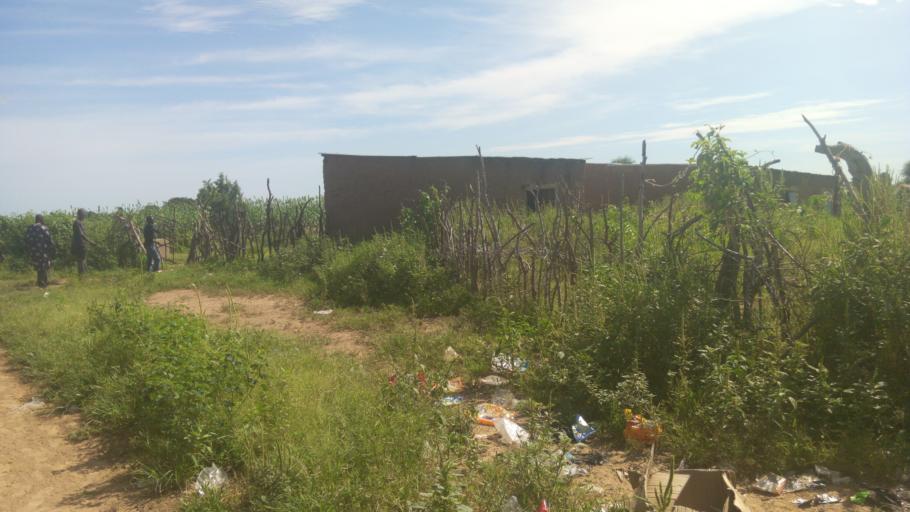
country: ML
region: Kayes
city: Yelimane
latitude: 14.8444
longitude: -10.7478
